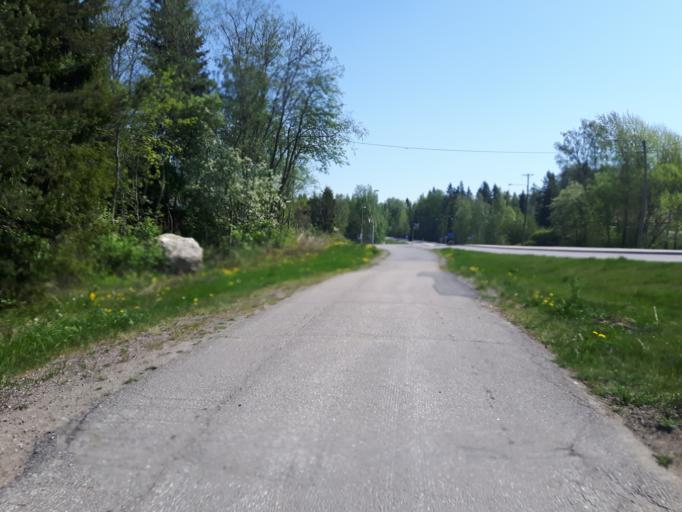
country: FI
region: Uusimaa
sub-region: Helsinki
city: Nickby
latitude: 60.2973
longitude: 25.3469
